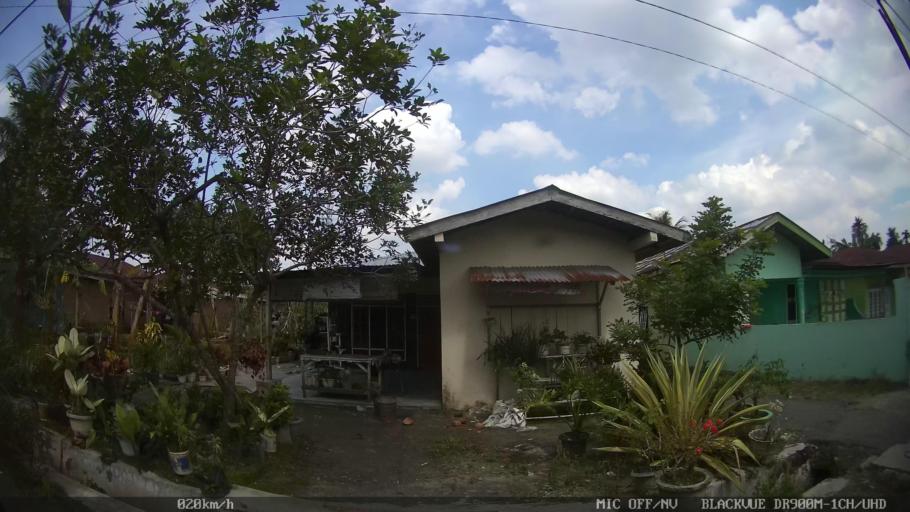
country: ID
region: North Sumatra
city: Binjai
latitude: 3.6263
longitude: 98.5171
